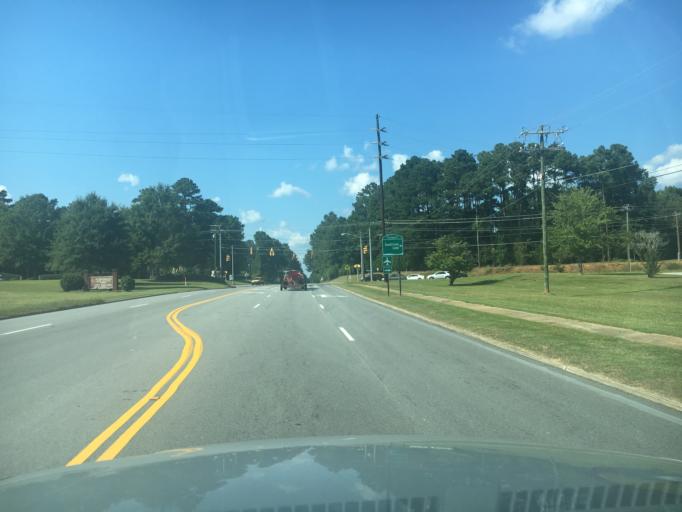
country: US
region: South Carolina
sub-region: Greenwood County
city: Greenwood
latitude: 34.2312
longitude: -82.1777
